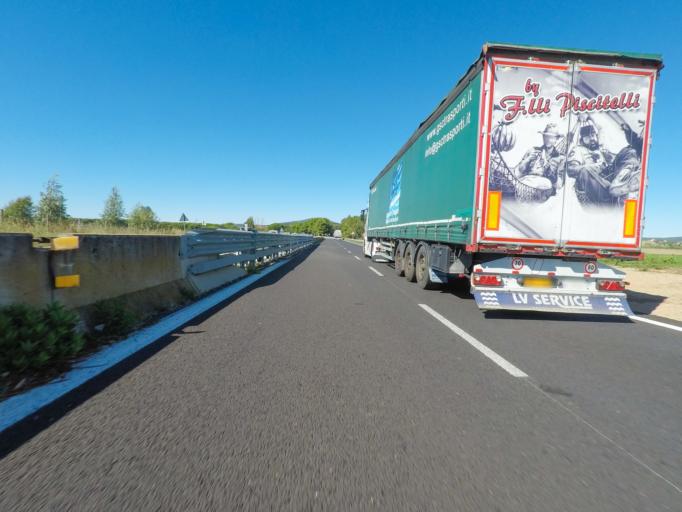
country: IT
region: Latium
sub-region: Provincia di Viterbo
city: Pescia Romana
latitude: 42.4106
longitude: 11.4773
